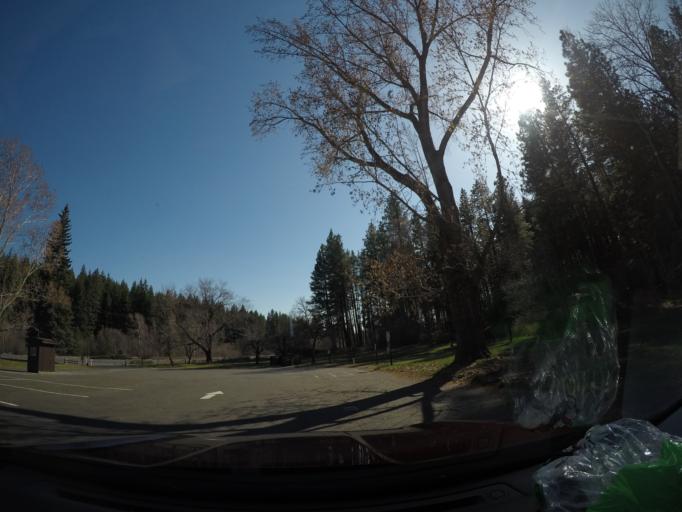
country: US
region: Washington
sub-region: Klickitat County
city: Goldendale
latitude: 45.9504
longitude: -120.6662
